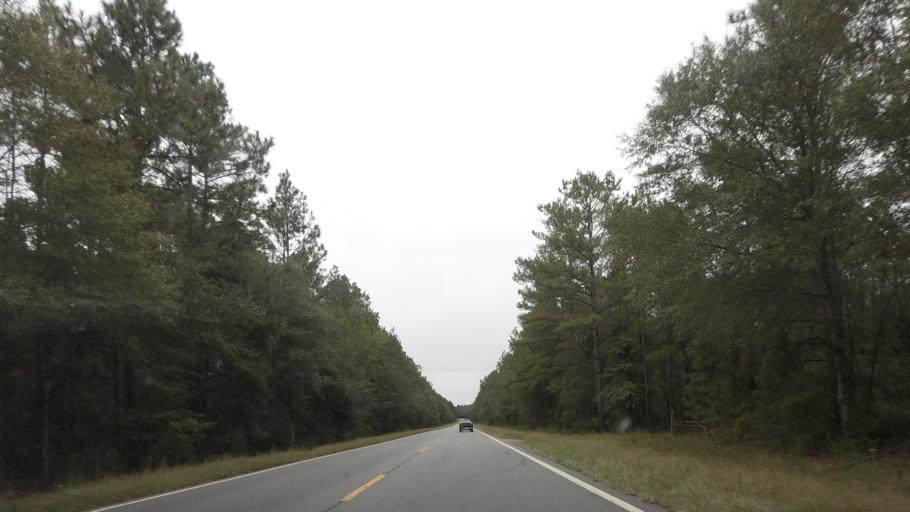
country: US
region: Georgia
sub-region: Berrien County
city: Enigma
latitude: 31.4114
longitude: -83.2424
